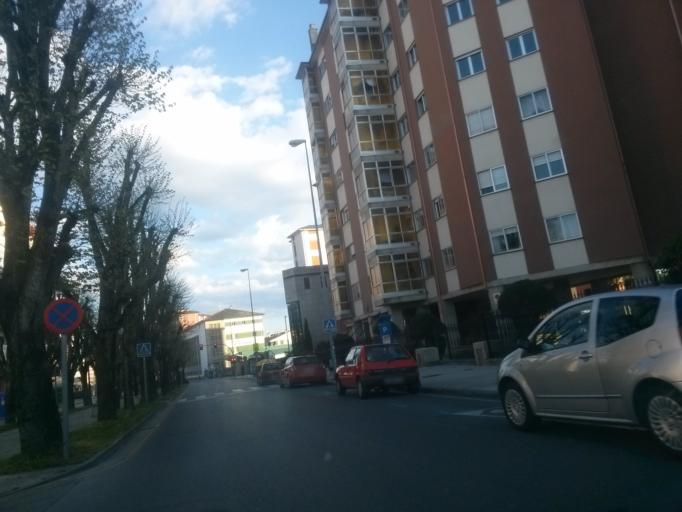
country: ES
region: Galicia
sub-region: Provincia de Lugo
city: Lugo
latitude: 43.0039
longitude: -7.5538
